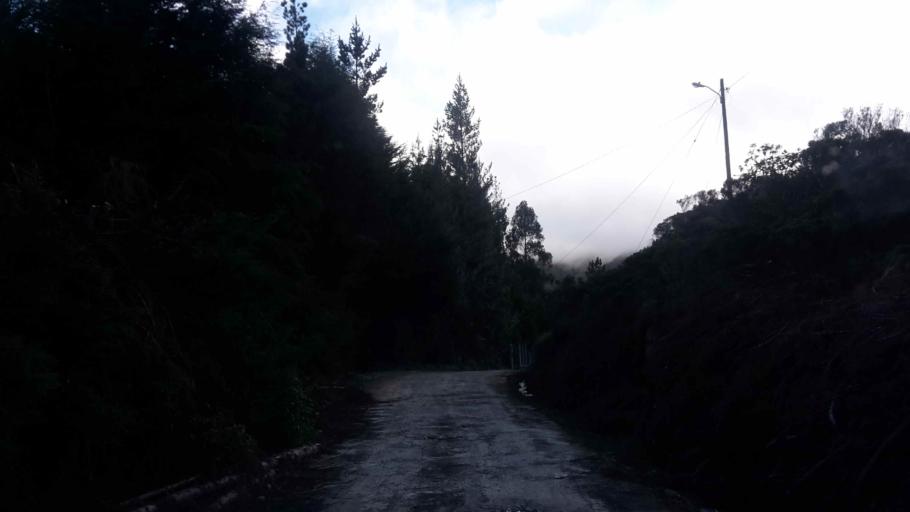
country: BO
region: Cochabamba
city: Colomi
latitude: -17.2372
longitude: -65.9008
